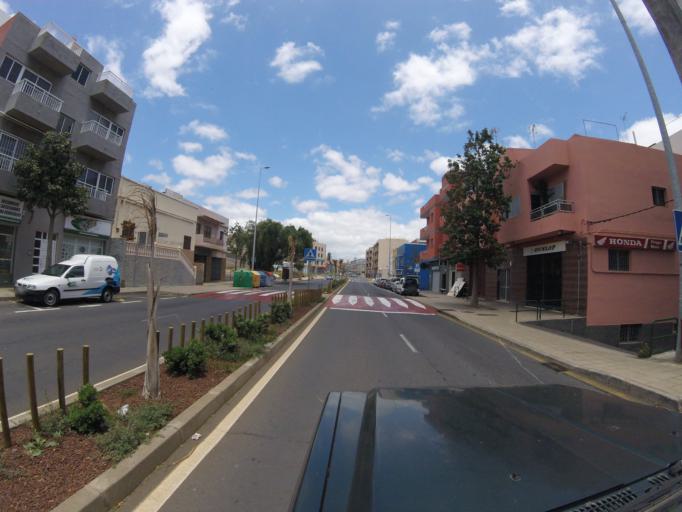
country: ES
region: Canary Islands
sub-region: Provincia de Santa Cruz de Tenerife
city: La Laguna
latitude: 28.4430
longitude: -16.3013
